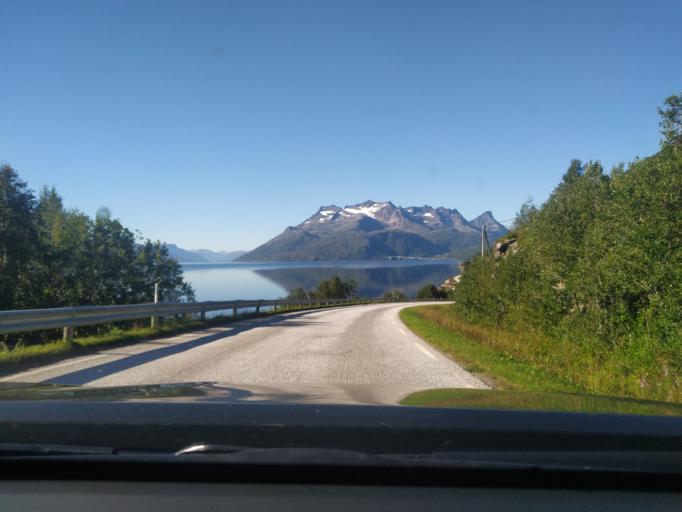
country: NO
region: Troms
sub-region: Dyroy
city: Brostadbotn
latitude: 68.9234
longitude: 17.6365
